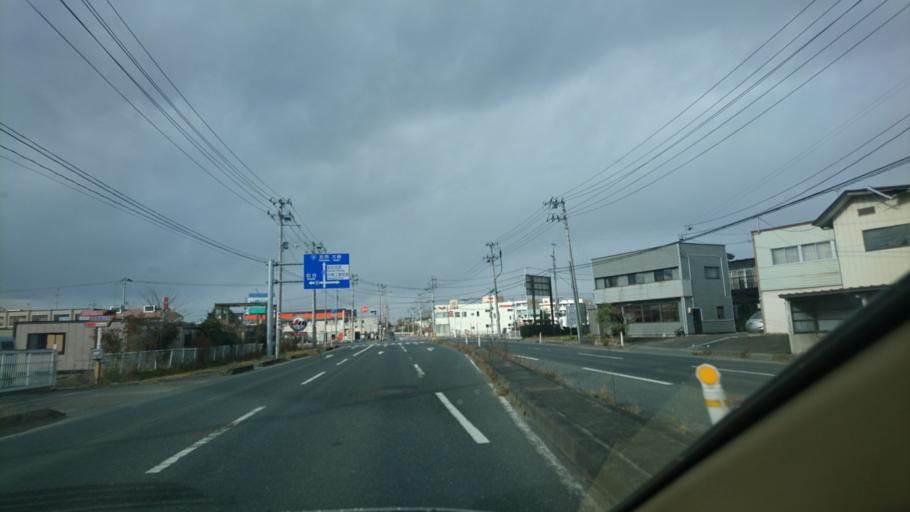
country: JP
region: Miyagi
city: Tomiya
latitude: 38.4388
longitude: 140.9062
